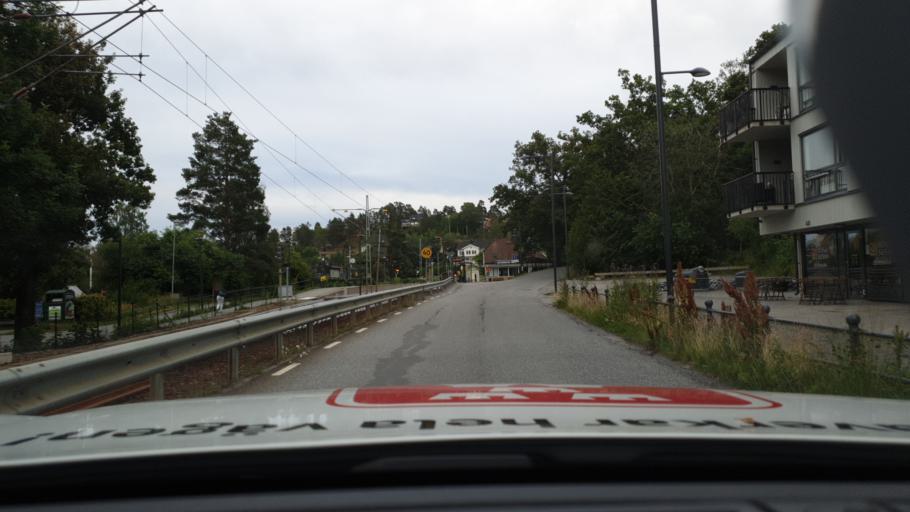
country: SE
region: Stockholm
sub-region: Osterakers Kommun
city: Akersberga
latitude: 59.4623
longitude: 18.3097
